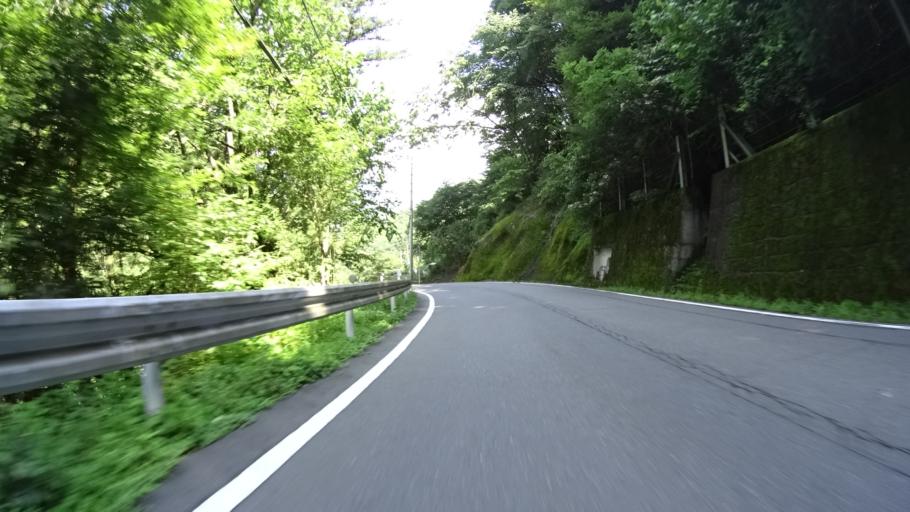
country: JP
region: Gunma
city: Tomioka
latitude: 36.0684
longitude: 138.8314
